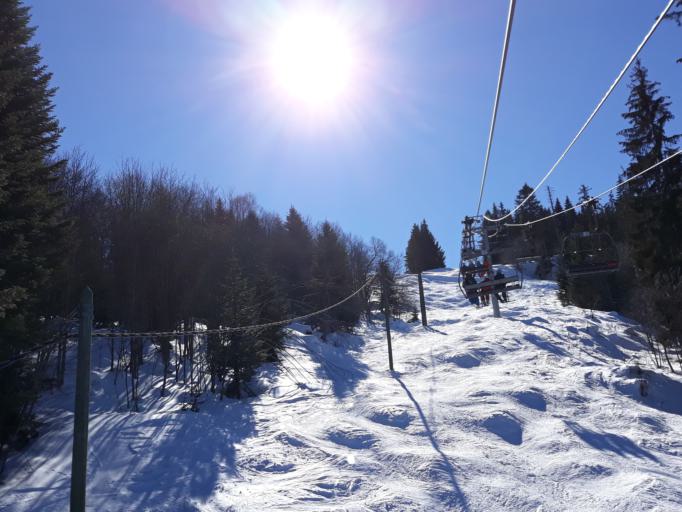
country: FR
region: Rhone-Alpes
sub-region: Departement de la Haute-Savoie
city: Araches-la-Frasse
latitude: 46.0551
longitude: 6.6704
